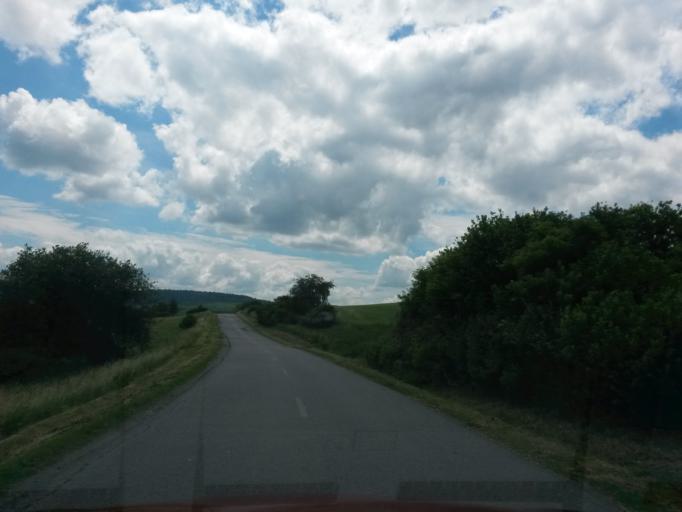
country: SK
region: Kosicky
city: Gelnica
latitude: 48.9341
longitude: 21.0454
